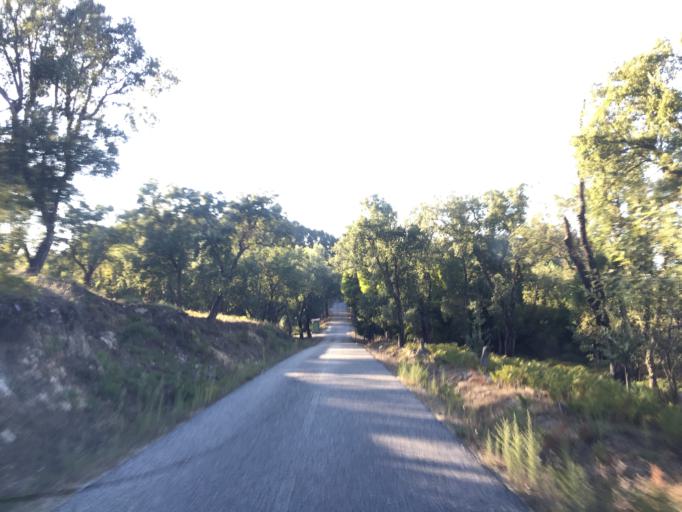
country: PT
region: Portalegre
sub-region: Castelo de Vide
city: Castelo de Vide
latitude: 39.4079
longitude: -7.4629
